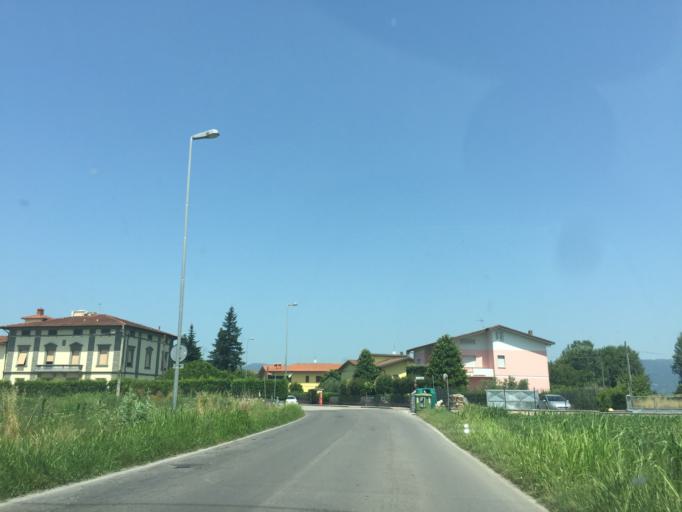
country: IT
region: Tuscany
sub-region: Provincia di Pistoia
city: Ponte Buggianese
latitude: 43.8355
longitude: 10.7519
